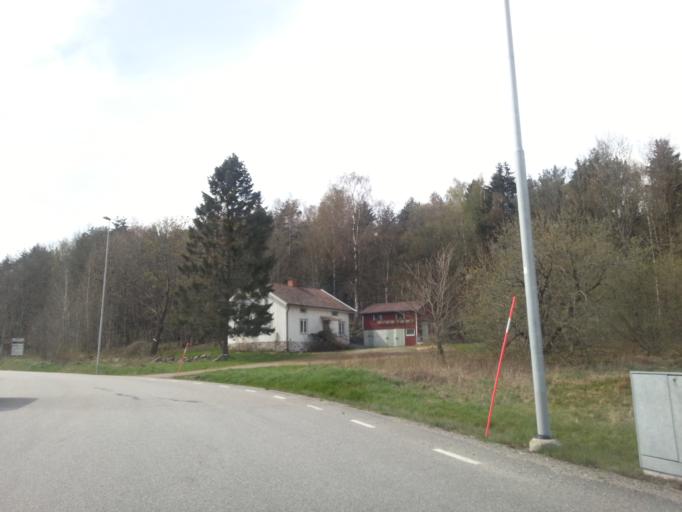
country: SE
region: Vaestra Goetaland
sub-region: Kungalvs Kommun
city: Kungalv
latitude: 57.8790
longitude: 11.9411
